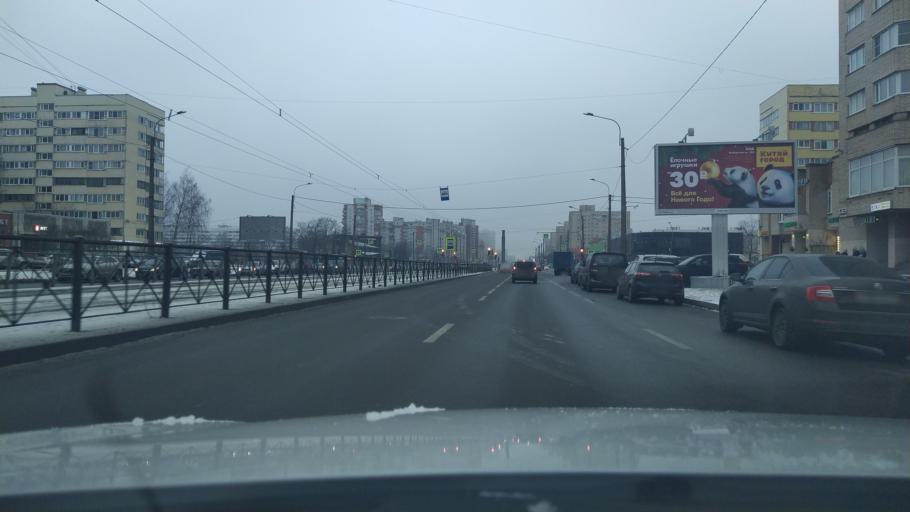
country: RU
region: St.-Petersburg
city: Grazhdanka
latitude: 60.0409
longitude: 30.3942
